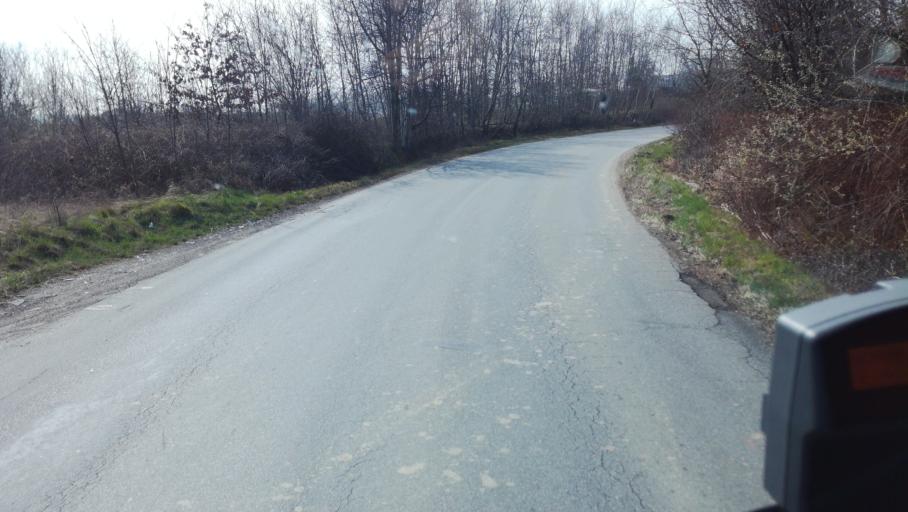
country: IT
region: Piedmont
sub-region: Provincia di Novara
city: Romagnano Sesia
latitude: 45.6349
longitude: 8.4026
